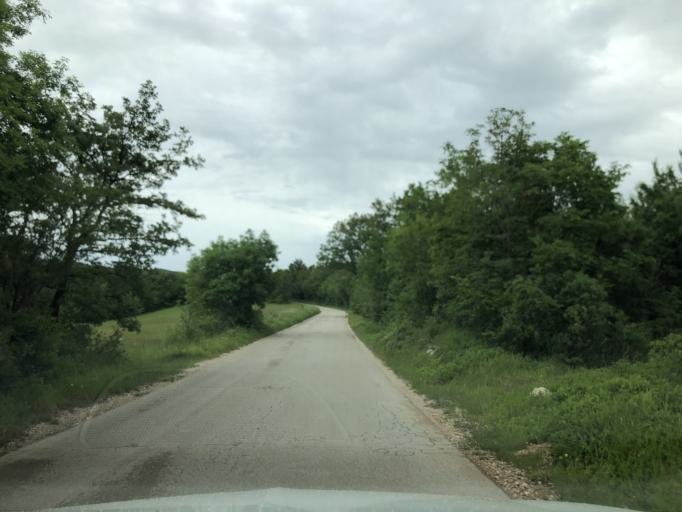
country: HR
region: Istarska
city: Buje
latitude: 45.4355
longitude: 13.6765
